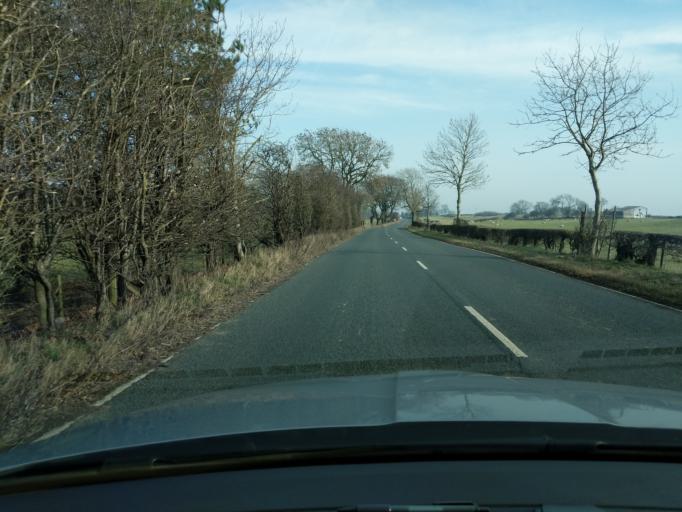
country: GB
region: England
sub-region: North Yorkshire
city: Catterick Garrison
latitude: 54.3462
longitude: -1.7372
